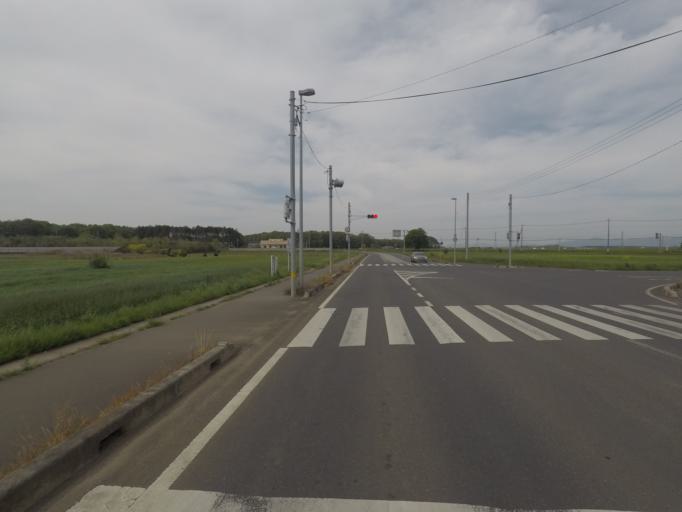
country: JP
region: Ibaraki
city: Makabe
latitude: 36.2372
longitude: 140.0327
